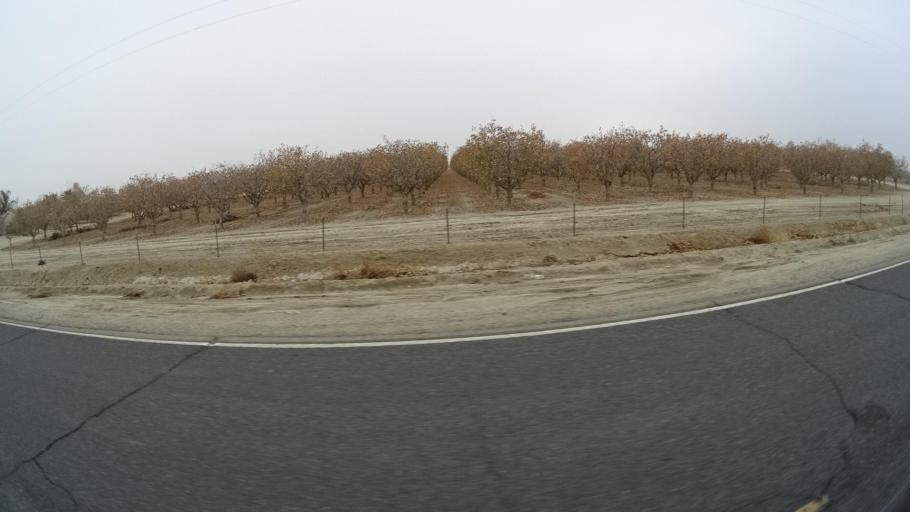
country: US
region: California
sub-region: Kern County
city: Buttonwillow
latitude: 35.3602
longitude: -119.4742
